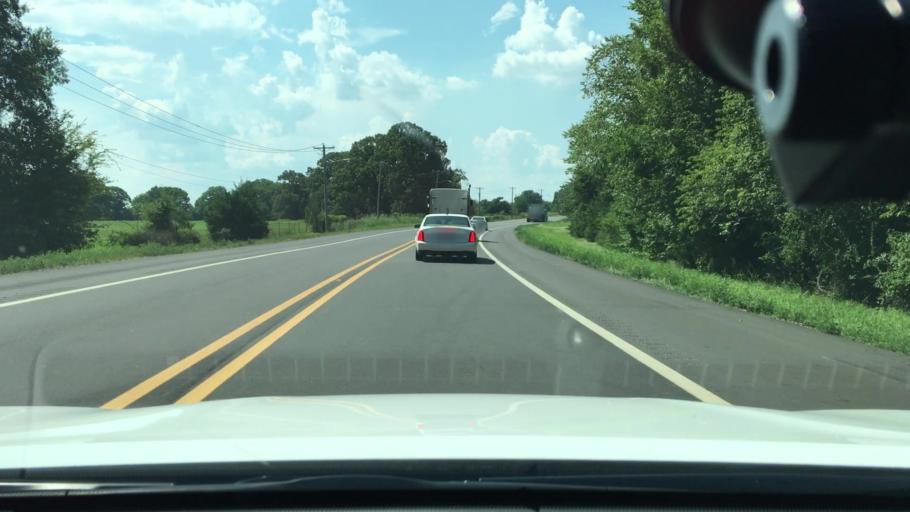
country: US
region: Arkansas
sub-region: Johnson County
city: Clarksville
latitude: 35.4537
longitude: -93.5326
